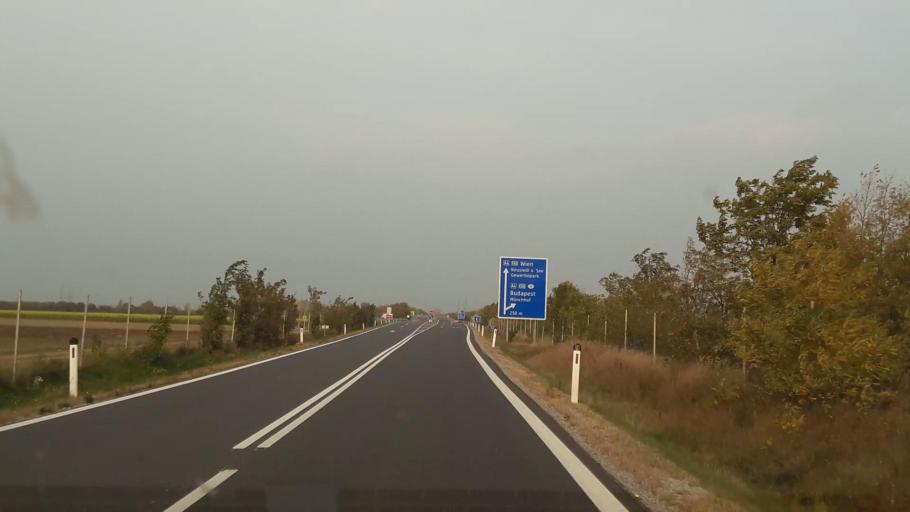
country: AT
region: Burgenland
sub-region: Politischer Bezirk Neusiedl am See
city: Gols
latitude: 47.9437
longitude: 16.9298
